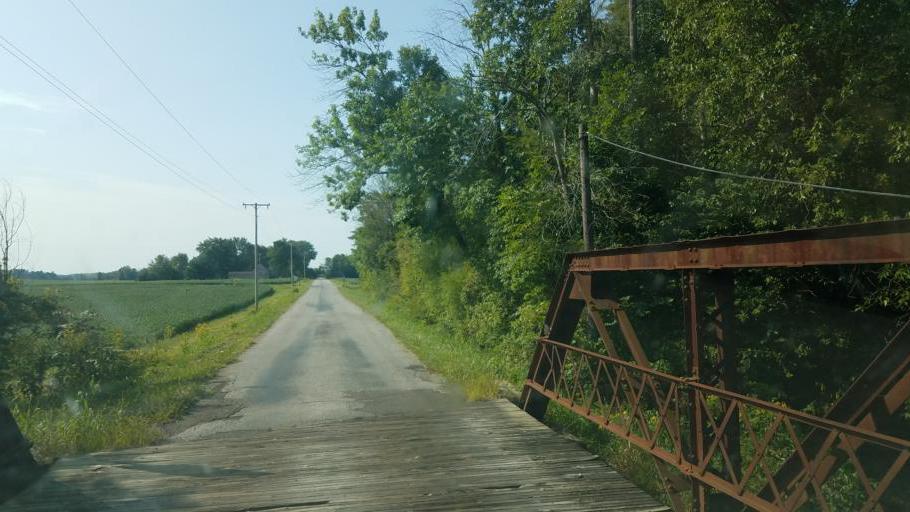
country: US
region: Ohio
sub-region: Morrow County
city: Cardington
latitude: 40.5444
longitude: -82.9194
